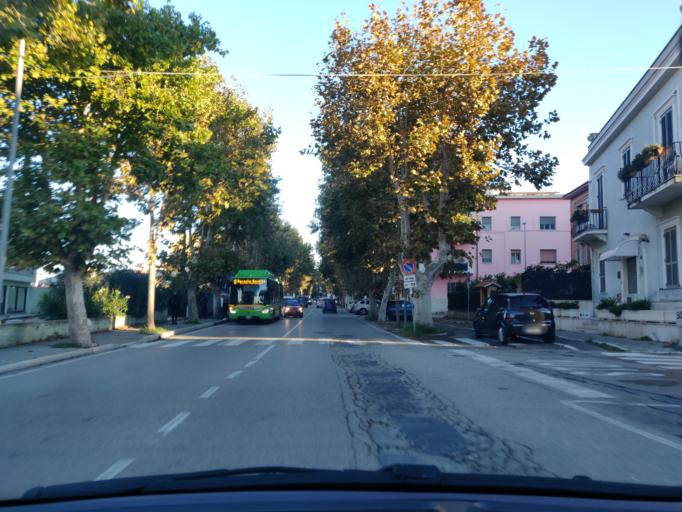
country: IT
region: Latium
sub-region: Citta metropolitana di Roma Capitale
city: Civitavecchia
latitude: 42.0849
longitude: 11.8052
